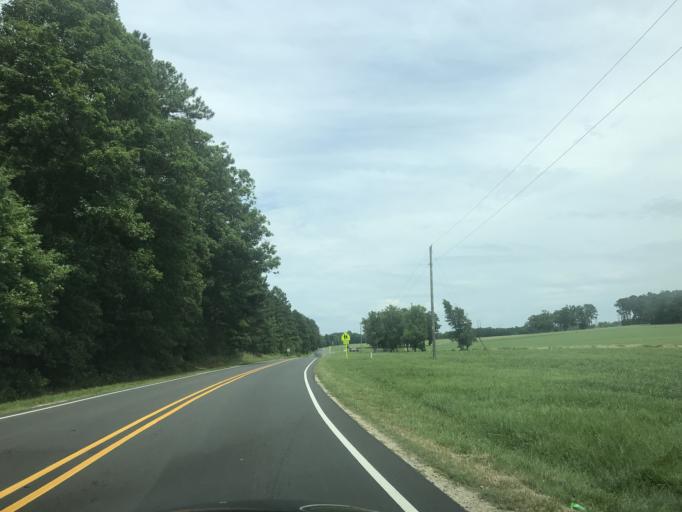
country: US
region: North Carolina
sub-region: Vance County
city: South Henderson
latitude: 36.2978
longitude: -78.4238
